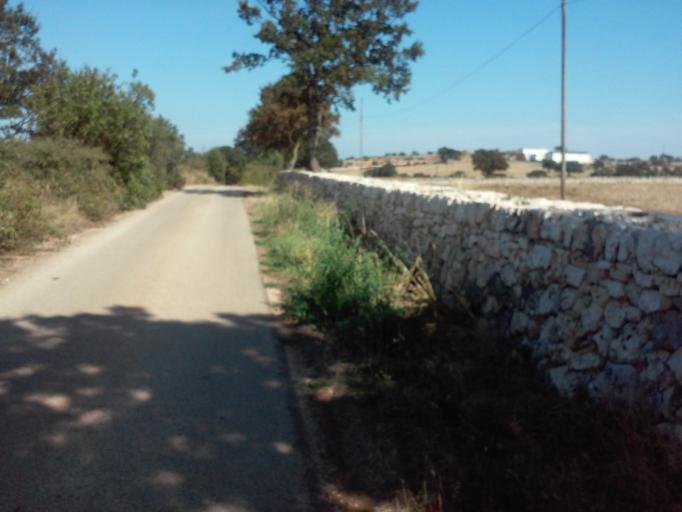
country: IT
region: Apulia
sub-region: Provincia di Bari
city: Turi
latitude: 40.8214
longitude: 17.0196
